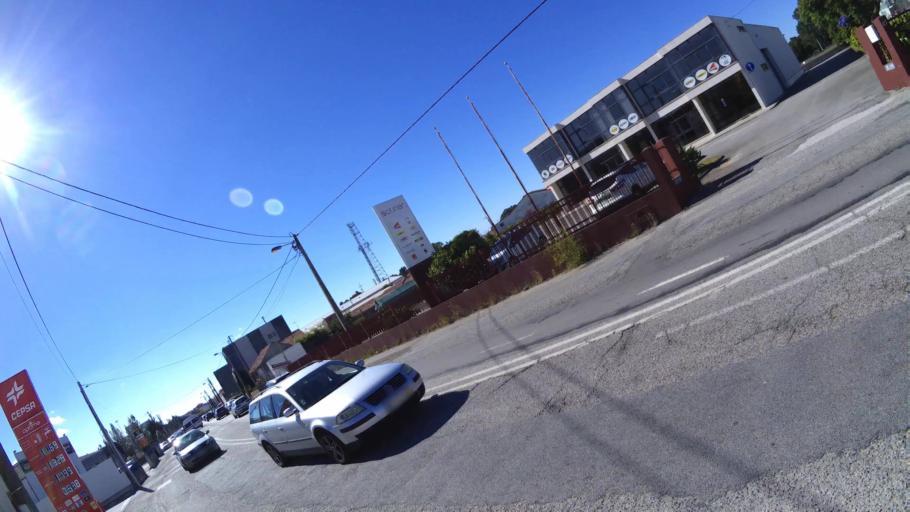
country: PT
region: Aveiro
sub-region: Aveiro
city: Aveiro
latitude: 40.6516
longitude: -8.6109
